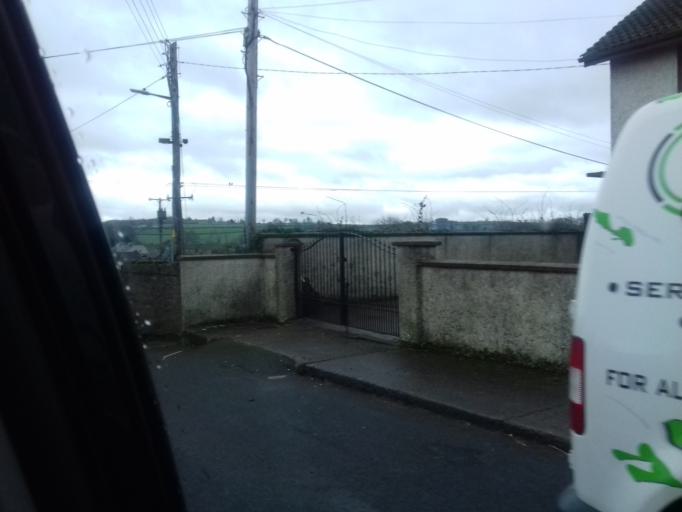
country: IE
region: Leinster
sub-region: County Carlow
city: Bagenalstown
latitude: 52.6292
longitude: -6.9962
